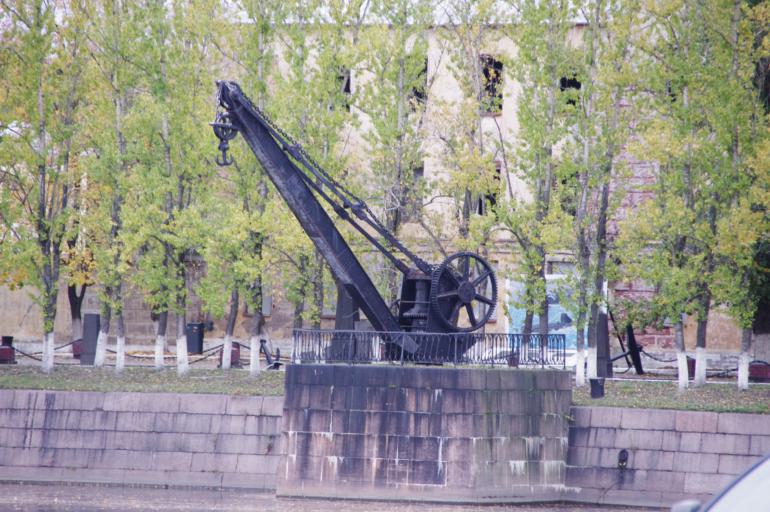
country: RU
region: St.-Petersburg
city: Kronshtadt
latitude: 59.9887
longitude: 29.7646
